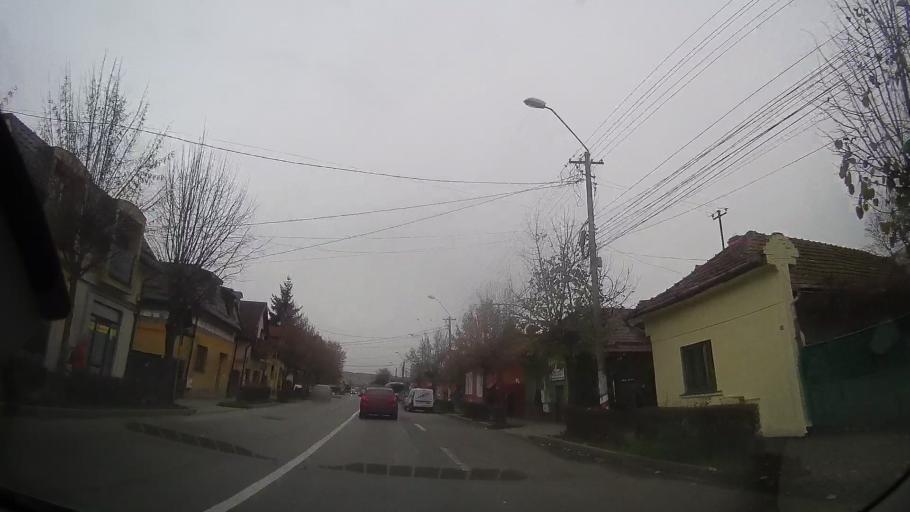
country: RO
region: Mures
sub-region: Comuna Santana de Mures
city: Santana de Mures
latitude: 46.5723
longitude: 24.5502
